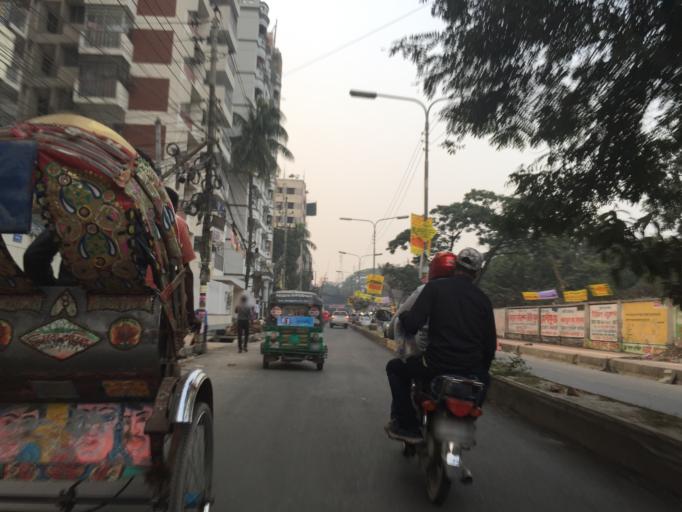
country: BD
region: Dhaka
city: Azimpur
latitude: 23.7656
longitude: 90.3650
